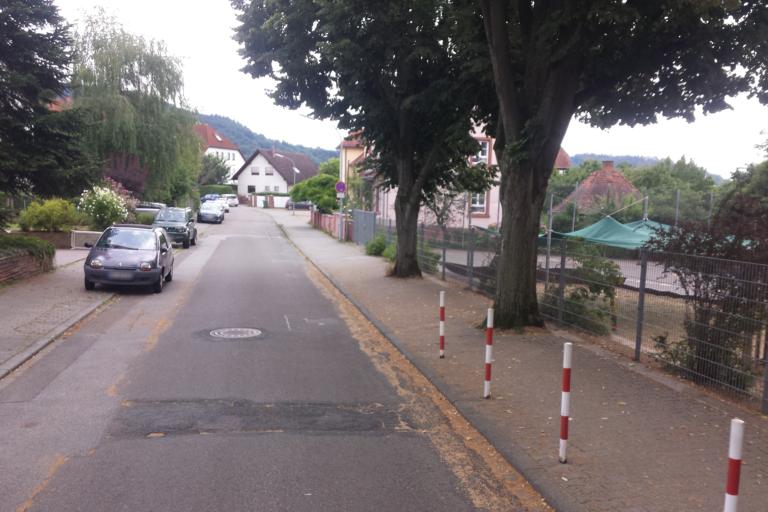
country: DE
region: Baden-Wuerttemberg
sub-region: Karlsruhe Region
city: Weinheim
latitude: 49.5605
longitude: 8.6695
